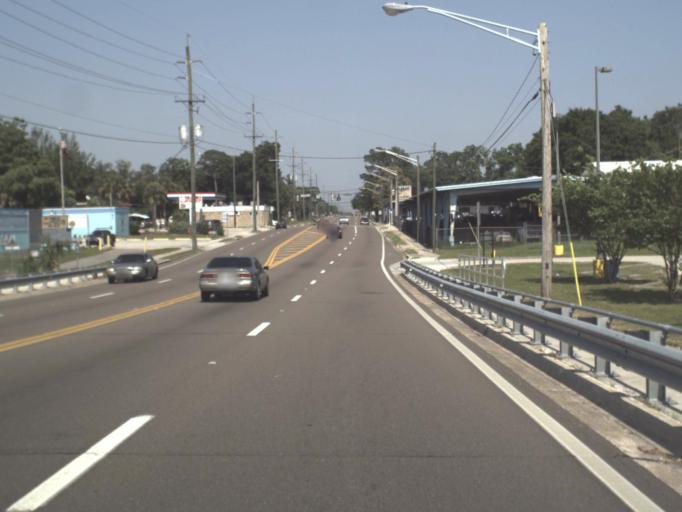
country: US
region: Florida
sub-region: Duval County
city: Jacksonville
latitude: 30.2820
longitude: -81.7401
